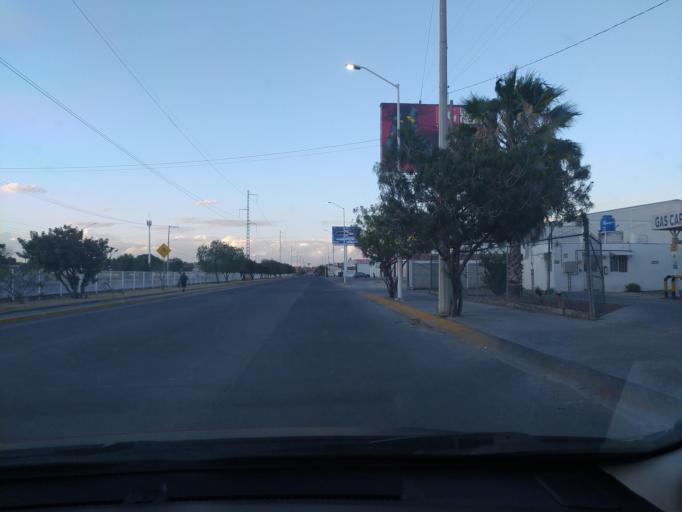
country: LA
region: Oudomxai
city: Muang La
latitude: 21.0215
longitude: 101.8694
